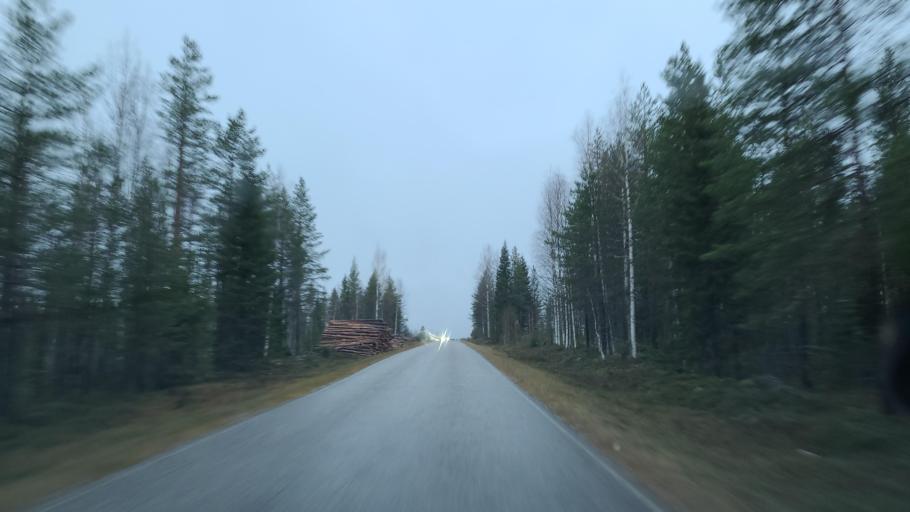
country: FI
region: Lapland
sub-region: Kemi-Tornio
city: Simo
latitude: 65.9090
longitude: 25.2029
